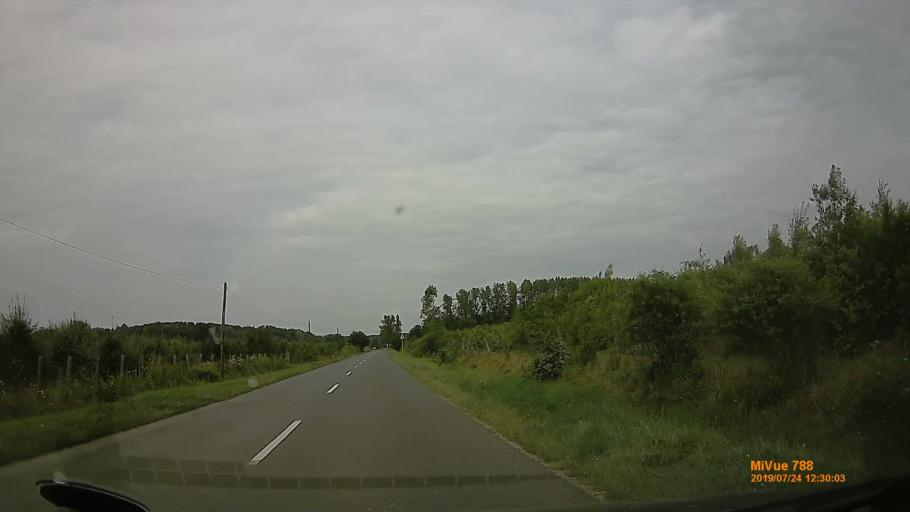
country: HU
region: Szabolcs-Szatmar-Bereg
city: Vasarosnameny
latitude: 48.1601
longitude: 22.3420
